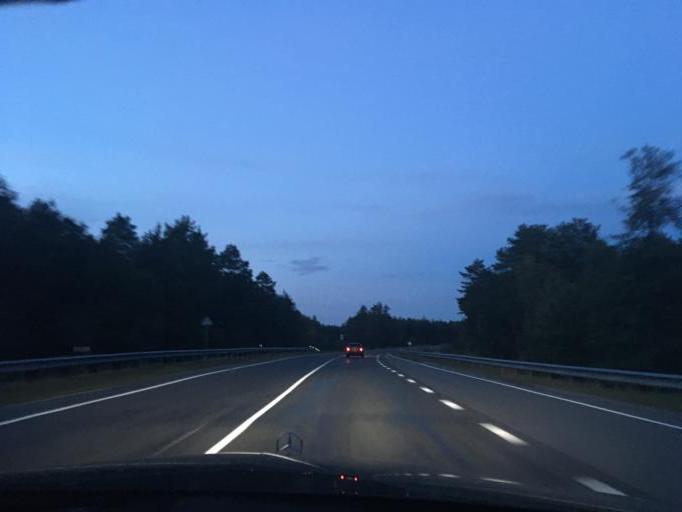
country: PL
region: Lublin Voivodeship
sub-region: Powiat bialski
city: Slawatycze
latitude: 51.7677
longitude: 23.6397
